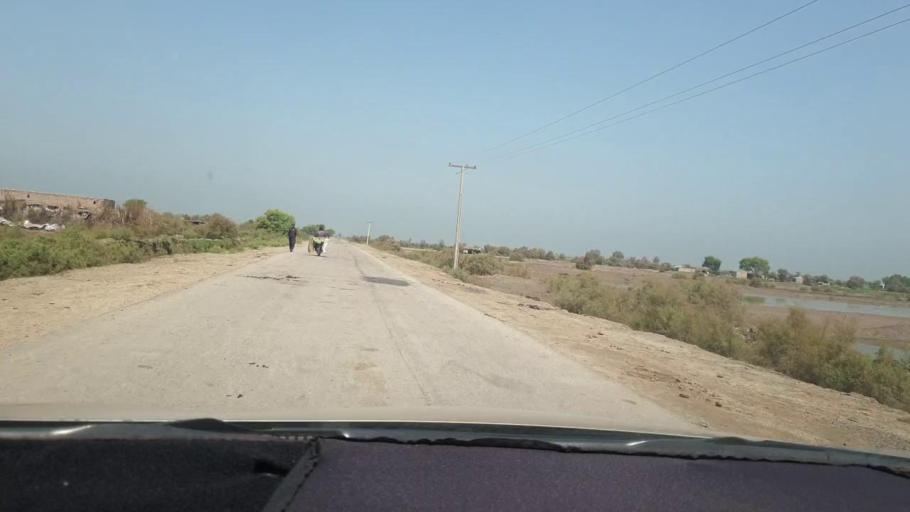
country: PK
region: Sindh
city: Miro Khan
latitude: 27.8249
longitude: 68.0199
